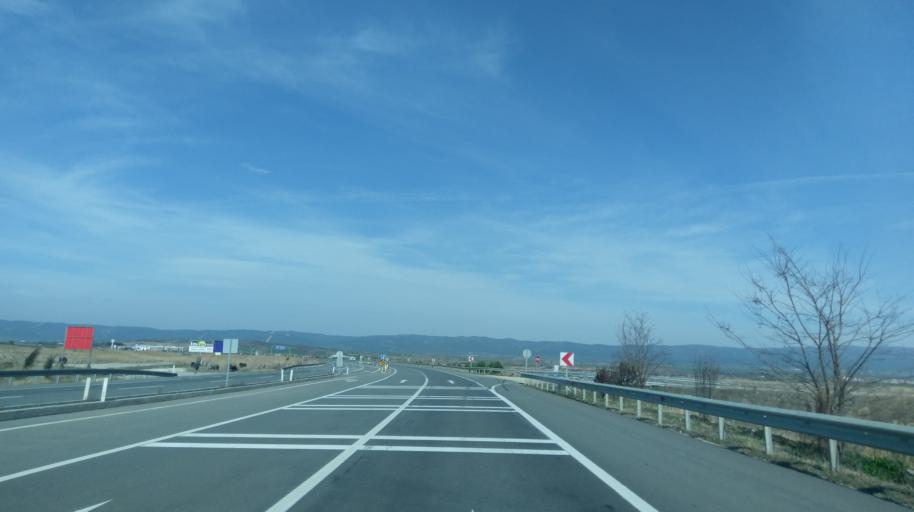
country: TR
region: Canakkale
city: Evrese
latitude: 40.6327
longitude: 26.8690
